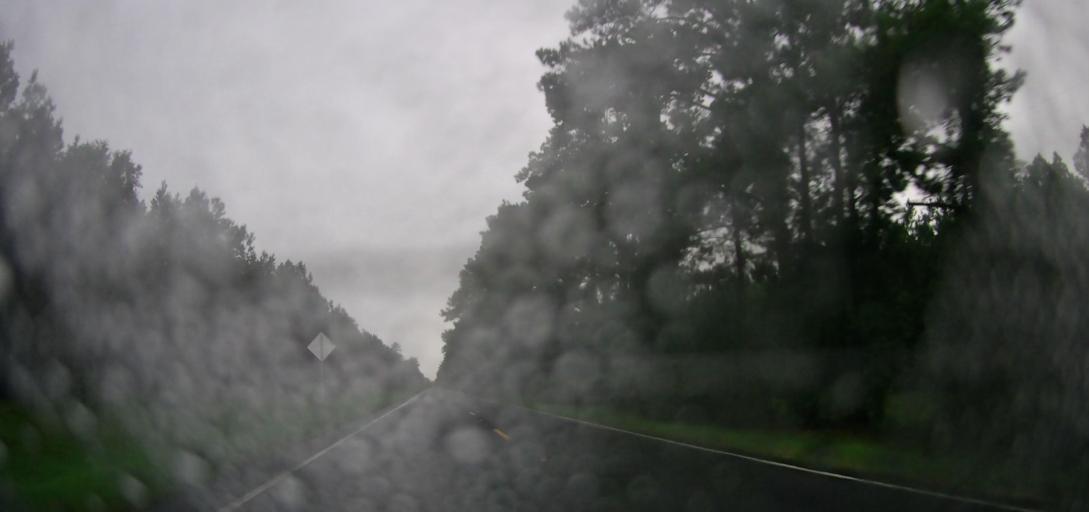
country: US
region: Georgia
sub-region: Glynn County
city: Dock Junction
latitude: 31.2710
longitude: -81.6441
